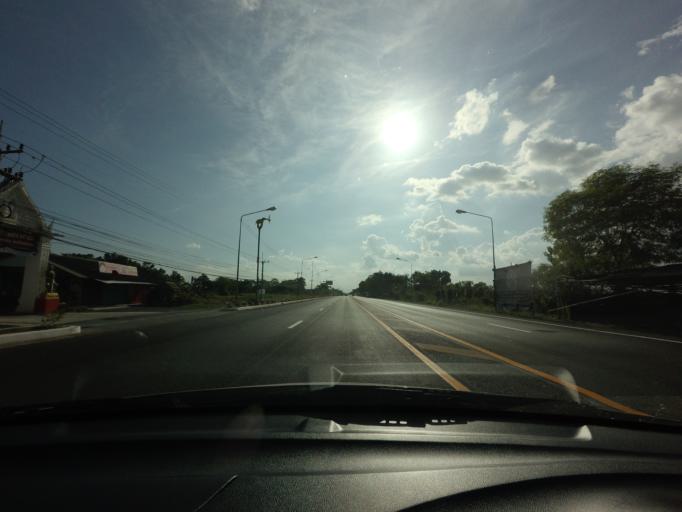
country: TH
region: Nakhon Nayok
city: Nakhon Nayok
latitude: 14.2372
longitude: 101.2444
